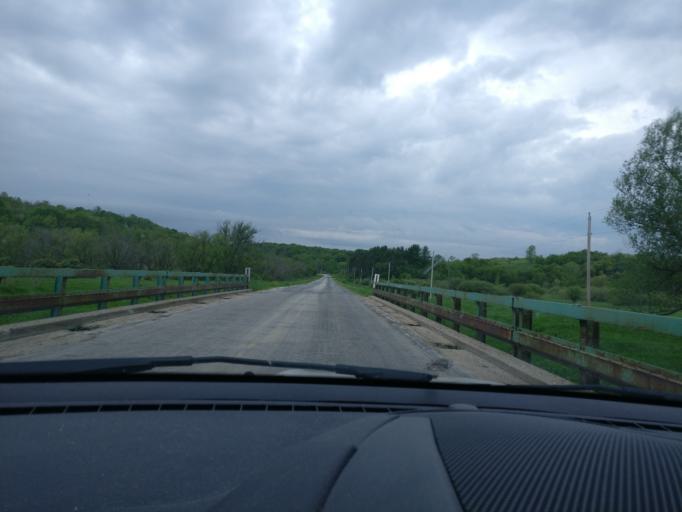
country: US
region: Wisconsin
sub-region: Lafayette County
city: Darlington
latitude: 42.7771
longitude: -89.9941
